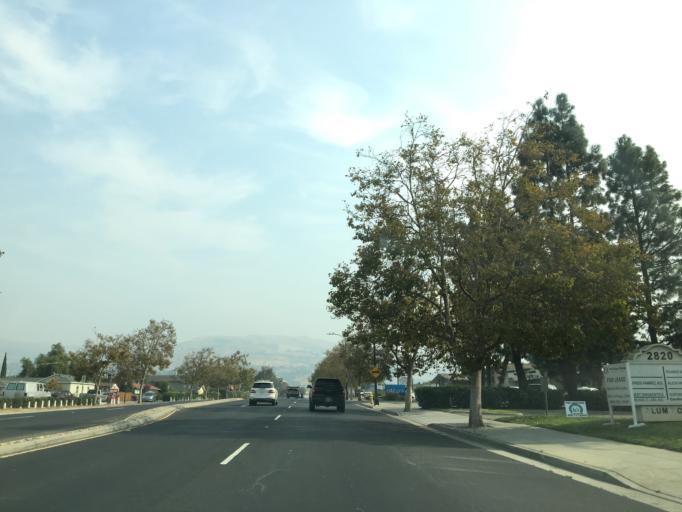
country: US
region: California
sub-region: Santa Clara County
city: Alum Rock
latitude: 37.3631
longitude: -121.8336
